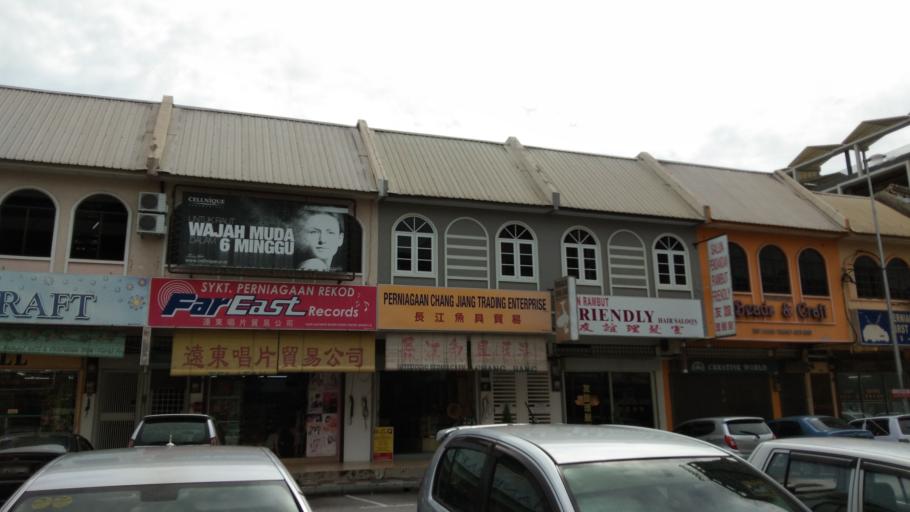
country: MY
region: Perak
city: Ipoh
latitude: 4.5944
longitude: 101.0845
